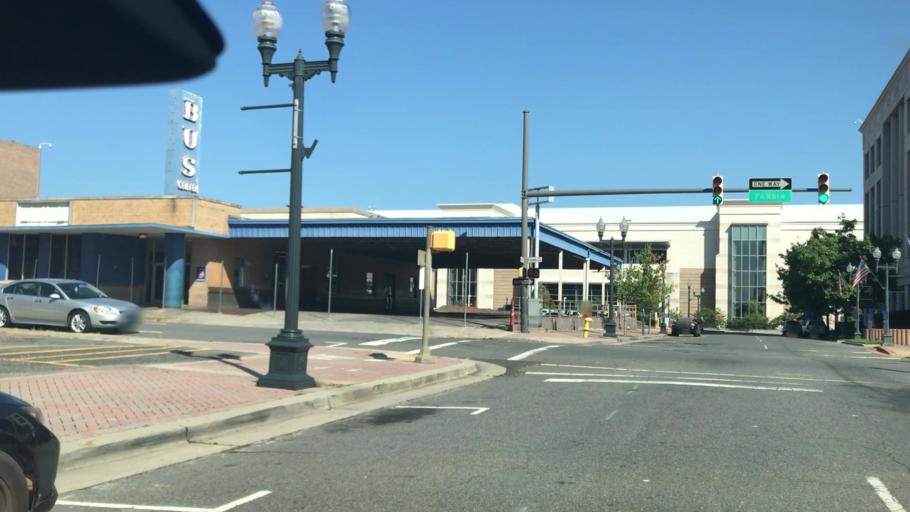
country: US
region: Louisiana
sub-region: Caddo Parish
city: Shreveport
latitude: 32.5151
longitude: -93.7503
